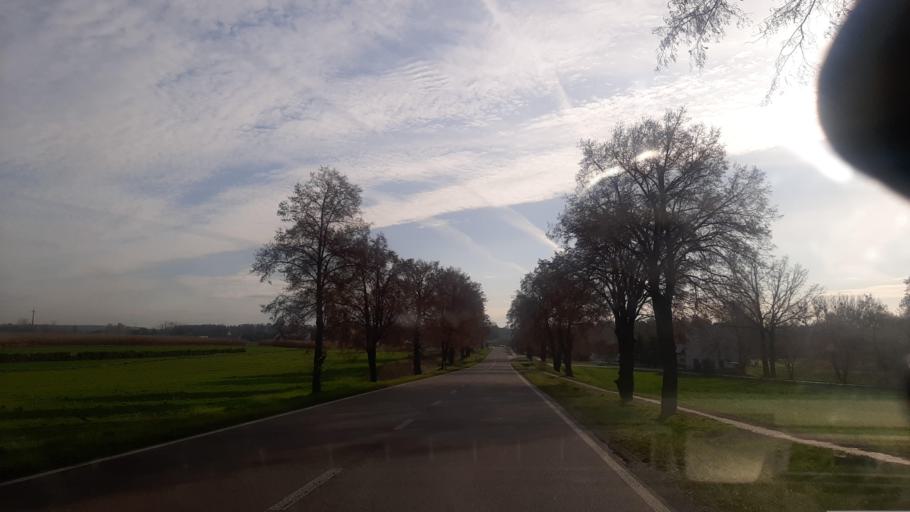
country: PL
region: Lublin Voivodeship
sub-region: Powiat pulawski
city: Markuszow
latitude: 51.3640
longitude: 22.2790
